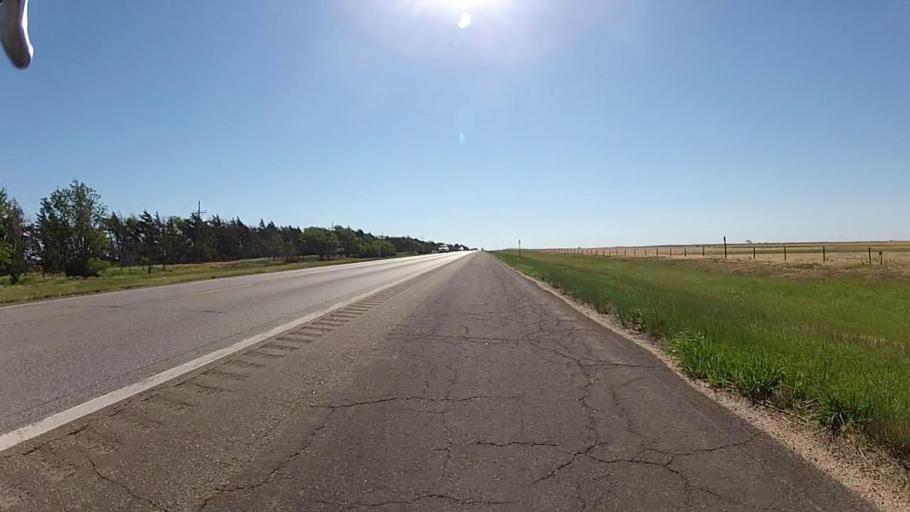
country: US
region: Kansas
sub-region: Kiowa County
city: Greensburg
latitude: 37.5865
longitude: -99.5816
